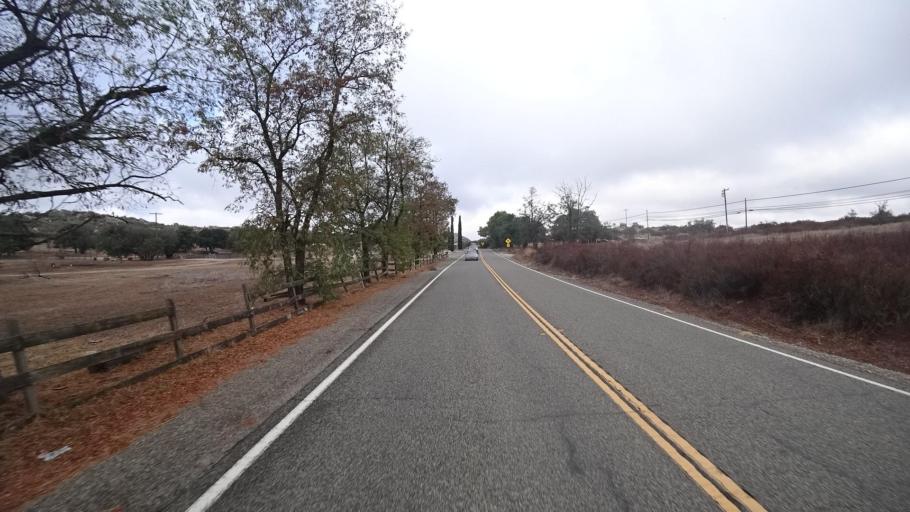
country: MX
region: Baja California
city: Tecate
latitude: 32.5996
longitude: -116.5828
